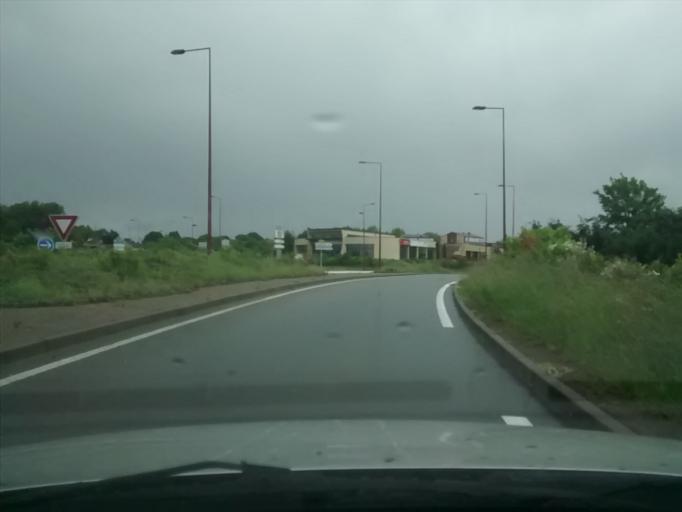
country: FR
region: Pays de la Loire
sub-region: Departement de la Sarthe
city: Coulaines
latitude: 48.0346
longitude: 0.2046
